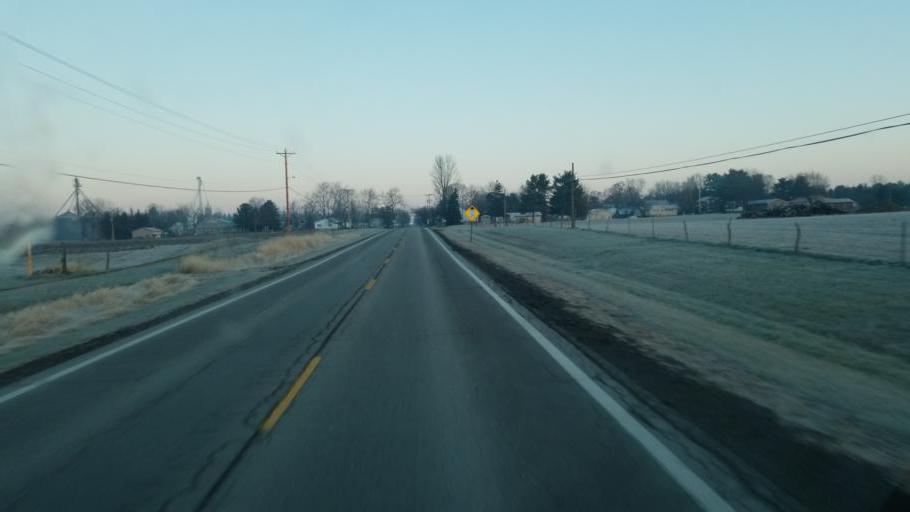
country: US
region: Ohio
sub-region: Wayne County
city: West Salem
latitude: 40.9644
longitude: -82.1096
